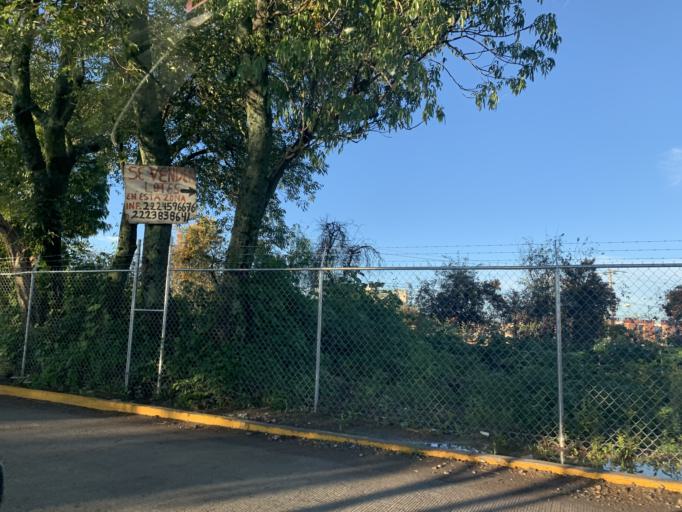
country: MX
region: Puebla
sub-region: Cuautlancingo
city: Sanctorum
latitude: 19.0904
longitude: -98.2479
